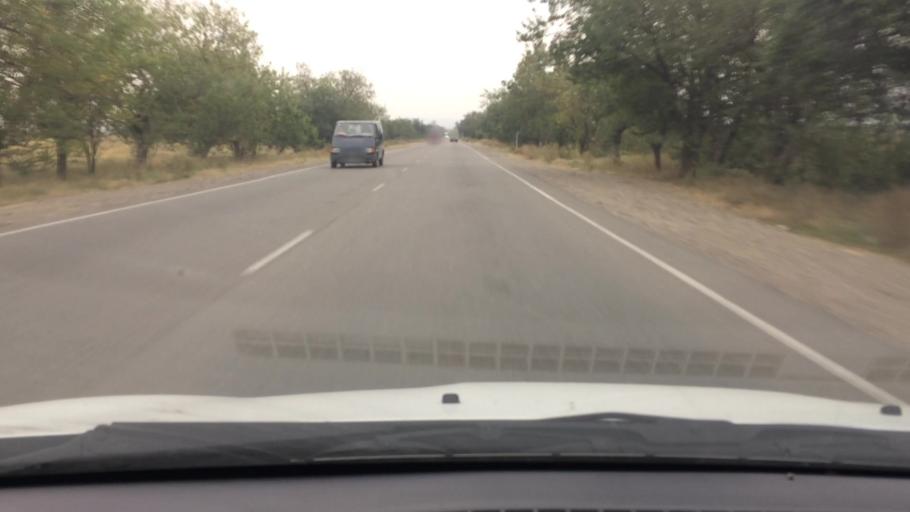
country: GE
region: Kvemo Kartli
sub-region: Marneuli
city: Marneuli
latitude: 41.5656
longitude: 44.7755
